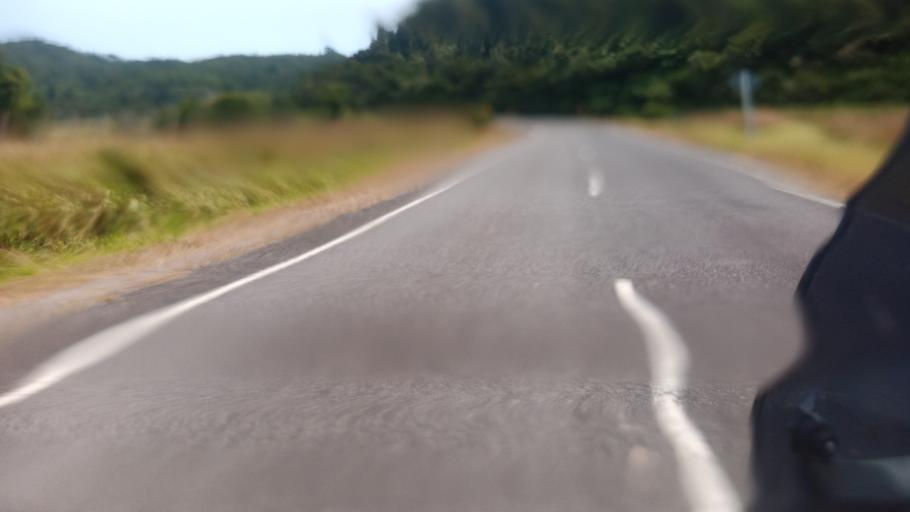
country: NZ
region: Bay of Plenty
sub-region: Opotiki District
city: Opotiki
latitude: -37.5756
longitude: 178.0288
